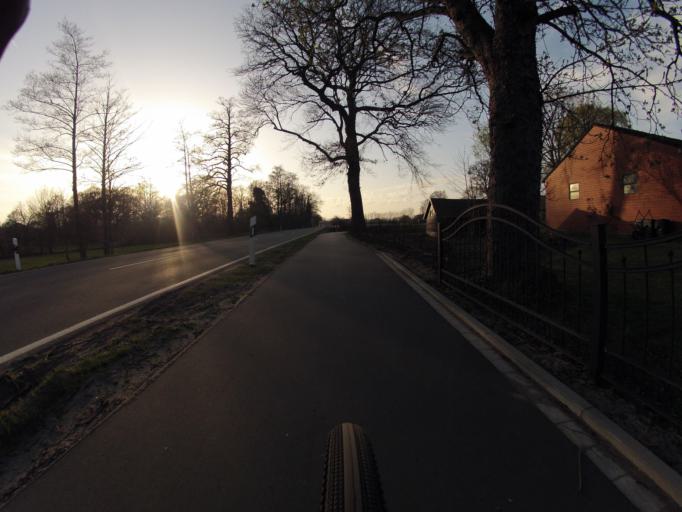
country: DE
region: North Rhine-Westphalia
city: Ibbenburen
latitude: 52.2305
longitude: 7.7112
